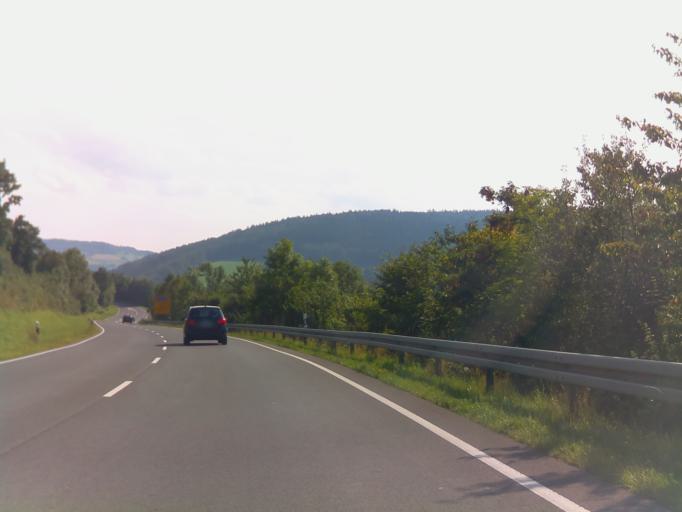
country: DE
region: Bavaria
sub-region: Regierungsbezirk Unterfranken
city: Wildflecken
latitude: 50.3587
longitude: 9.8883
